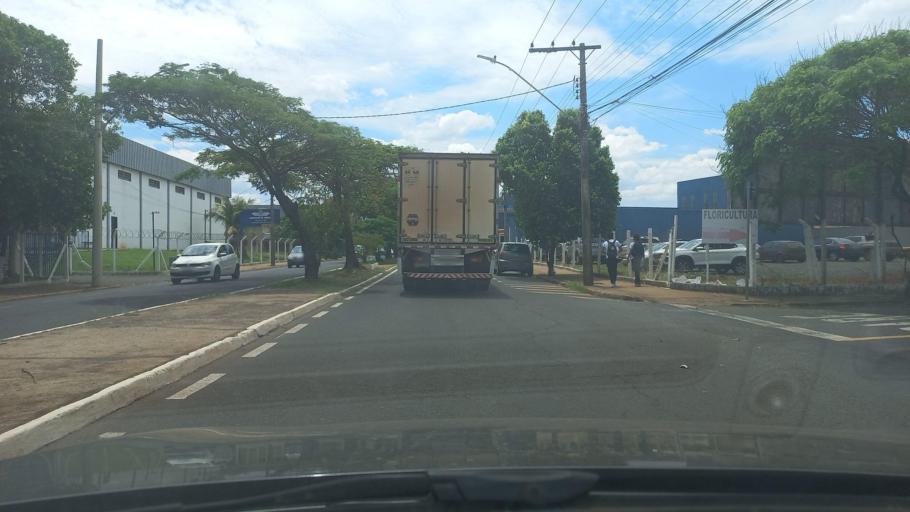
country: BR
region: Minas Gerais
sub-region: Uberaba
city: Uberaba
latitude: -19.7692
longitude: -47.9591
